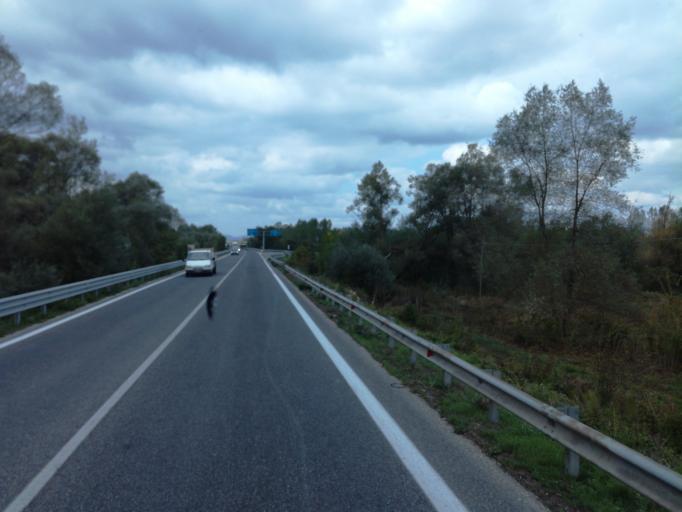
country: IT
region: Molise
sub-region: Provincia di Campobasso
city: San Polomatese
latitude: 41.4830
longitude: 14.4944
